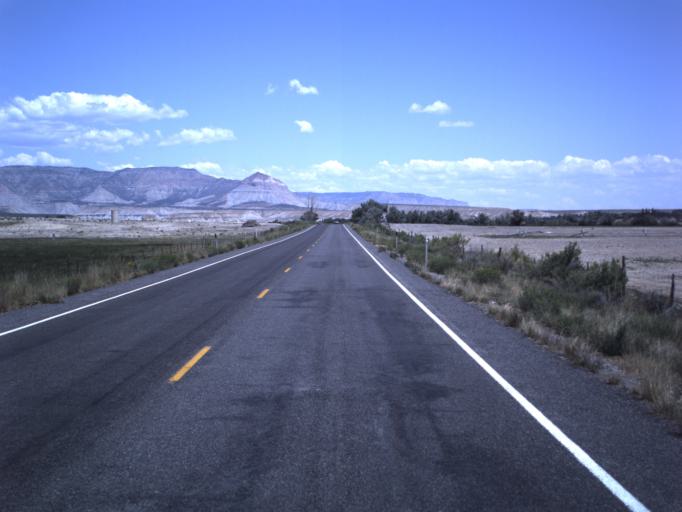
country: US
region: Utah
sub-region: Emery County
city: Orangeville
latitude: 39.2029
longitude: -111.0479
